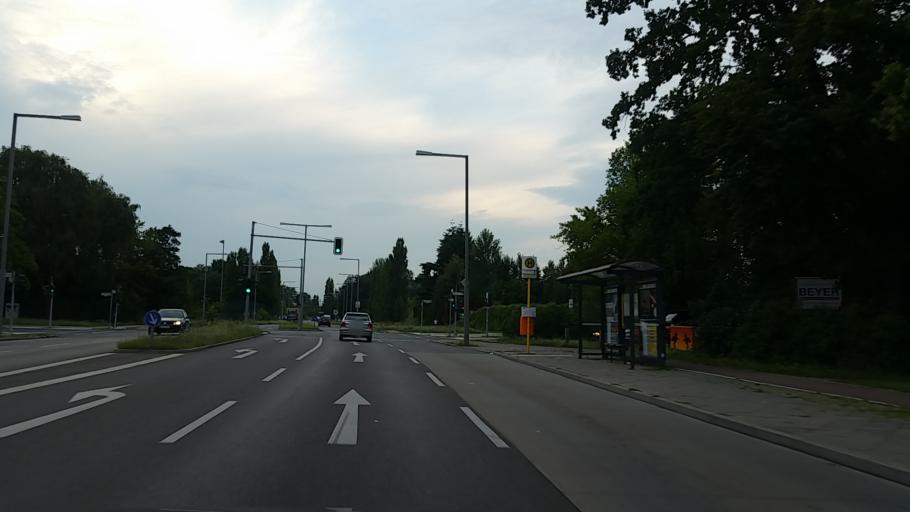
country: DE
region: Berlin
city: Haselhorst
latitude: 52.5463
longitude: 13.2309
